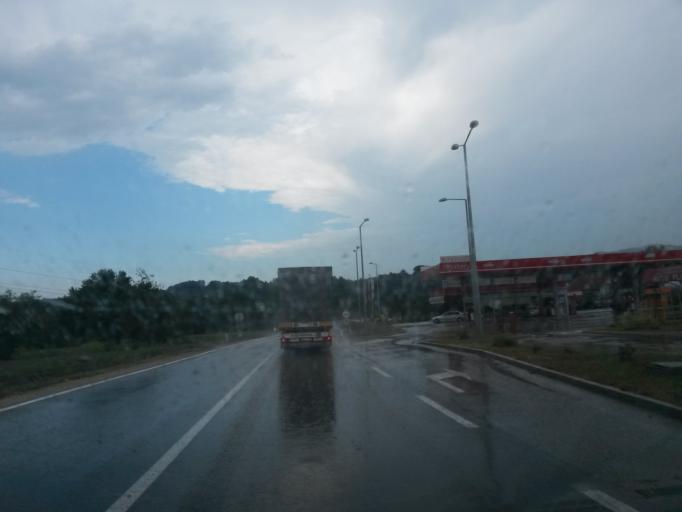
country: BA
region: Federation of Bosnia and Herzegovina
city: Lijesnica
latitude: 44.4809
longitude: 18.0683
